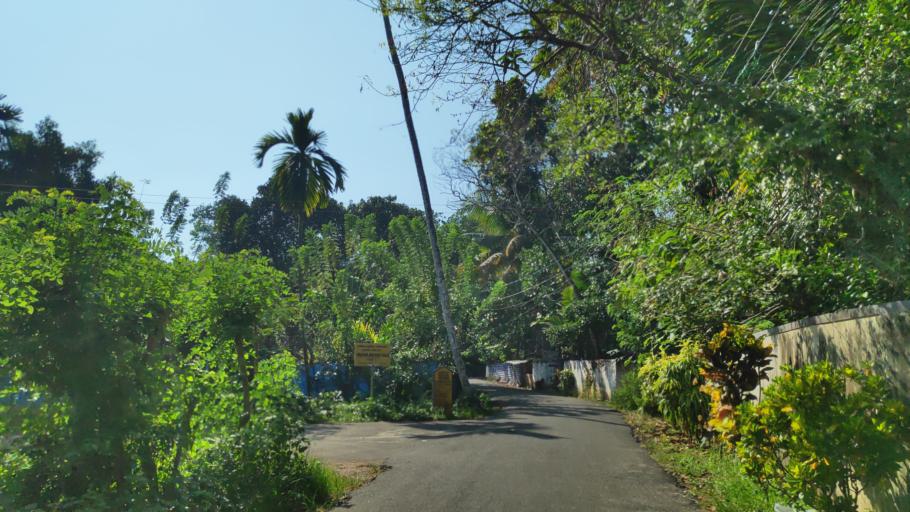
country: IN
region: Kerala
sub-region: Alappuzha
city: Alleppey
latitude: 9.5334
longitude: 76.3129
